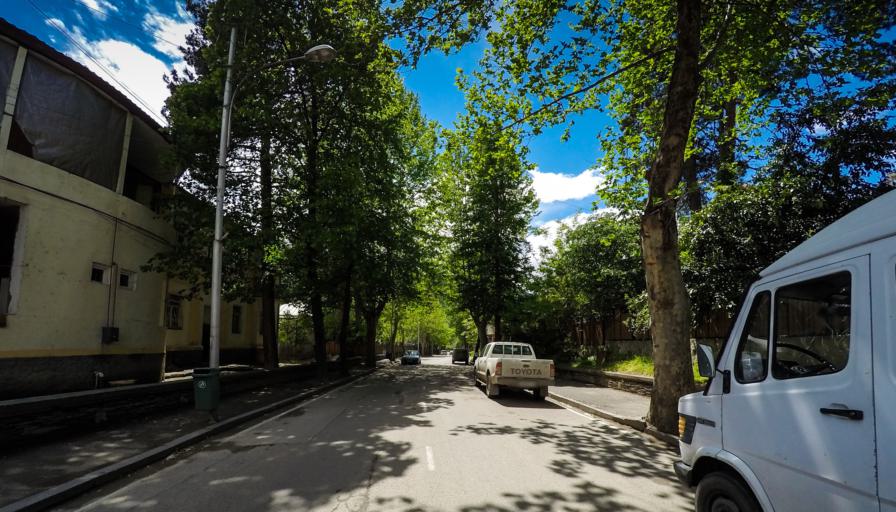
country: GE
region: Mtskheta-Mtianeti
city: Mtskheta
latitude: 41.8421
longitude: 44.7165
